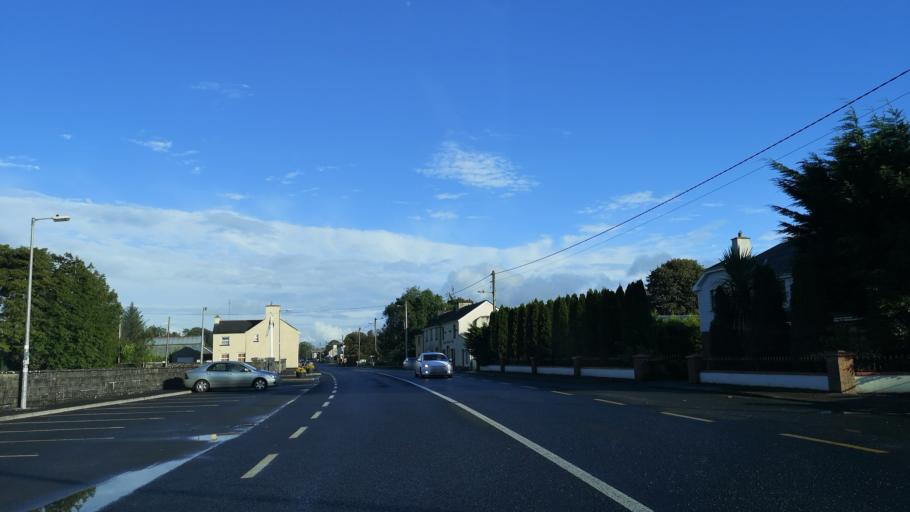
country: IE
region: Connaught
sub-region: Roscommon
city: Ballaghaderreen
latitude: 53.8232
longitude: -8.5653
